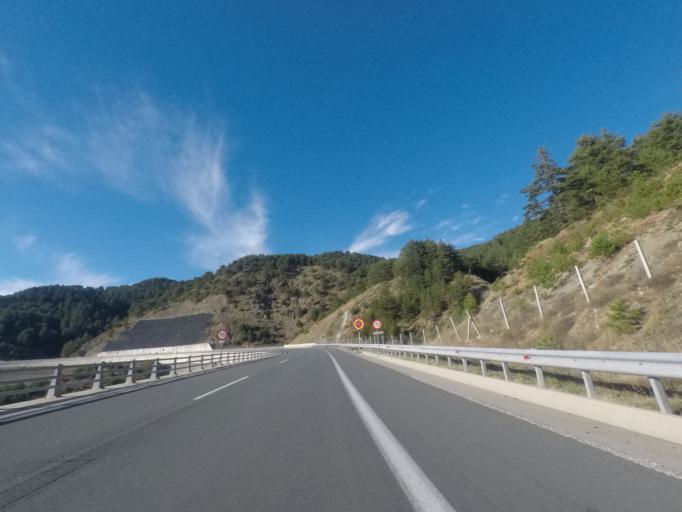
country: GR
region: Epirus
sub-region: Nomos Ioanninon
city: Metsovo
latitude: 39.7889
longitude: 21.2801
